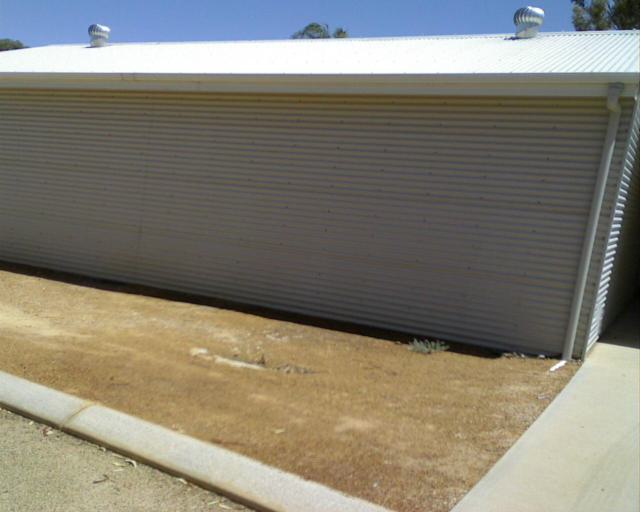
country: AU
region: Western Australia
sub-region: Wongan-Ballidu
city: Wongan Hills
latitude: -30.8246
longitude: 117.4844
